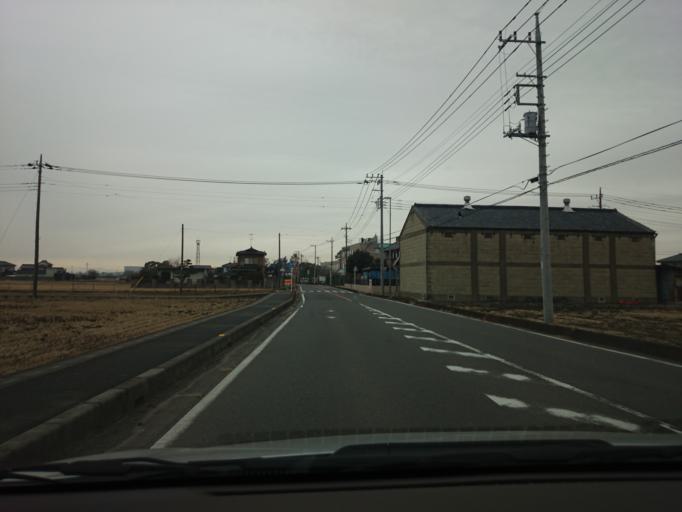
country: JP
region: Saitama
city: Kisai
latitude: 36.1107
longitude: 139.5865
